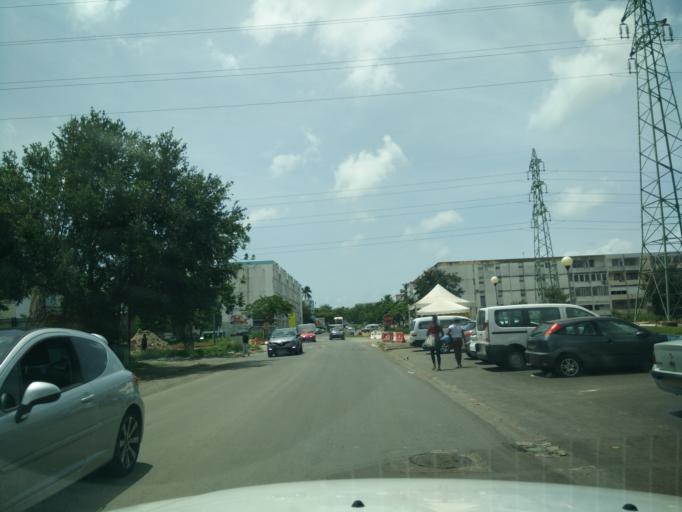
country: GP
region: Guadeloupe
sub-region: Guadeloupe
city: Pointe-a-Pitre
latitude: 16.2550
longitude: -61.5302
